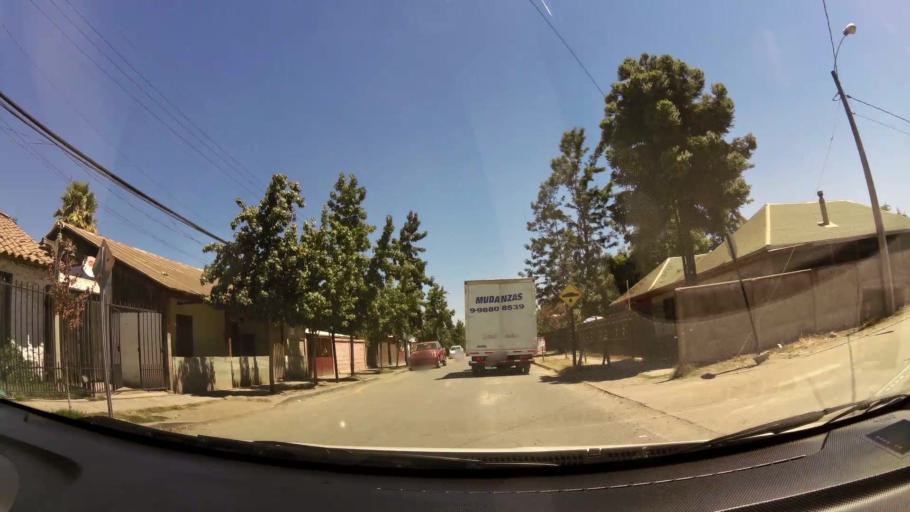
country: CL
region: O'Higgins
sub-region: Provincia de Cachapoal
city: Rancagua
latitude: -34.2244
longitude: -70.7866
